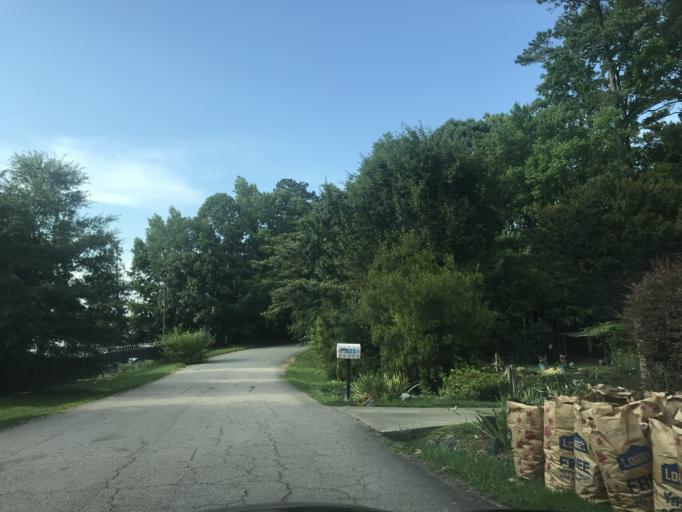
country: US
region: North Carolina
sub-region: Wake County
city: Raleigh
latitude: 35.8322
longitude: -78.5824
